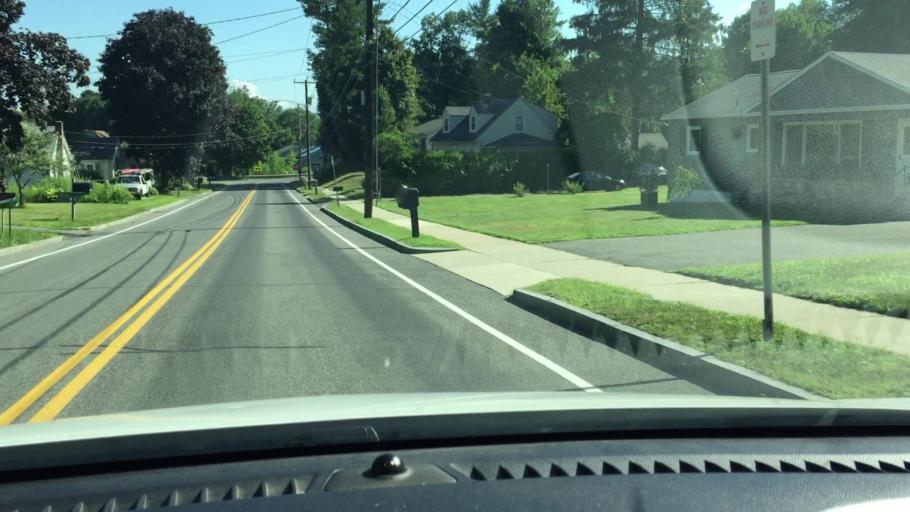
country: US
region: Massachusetts
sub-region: Berkshire County
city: Pittsfield
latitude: 42.4862
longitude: -73.2593
